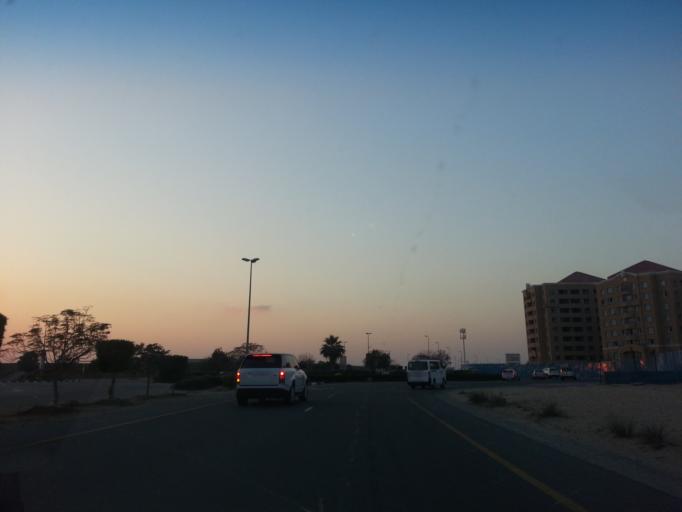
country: AE
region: Dubai
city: Dubai
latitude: 24.9887
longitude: 55.1834
